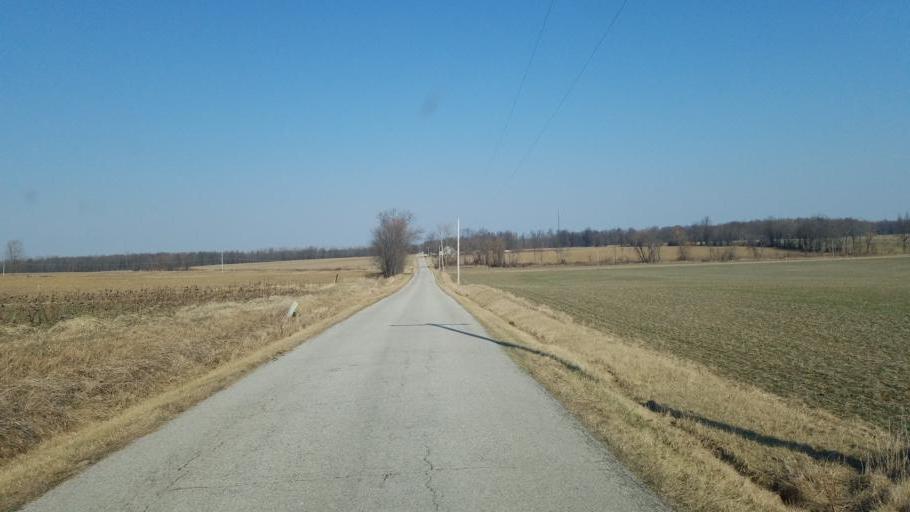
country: US
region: Ohio
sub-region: Crawford County
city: Crestline
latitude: 40.7673
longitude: -82.7652
